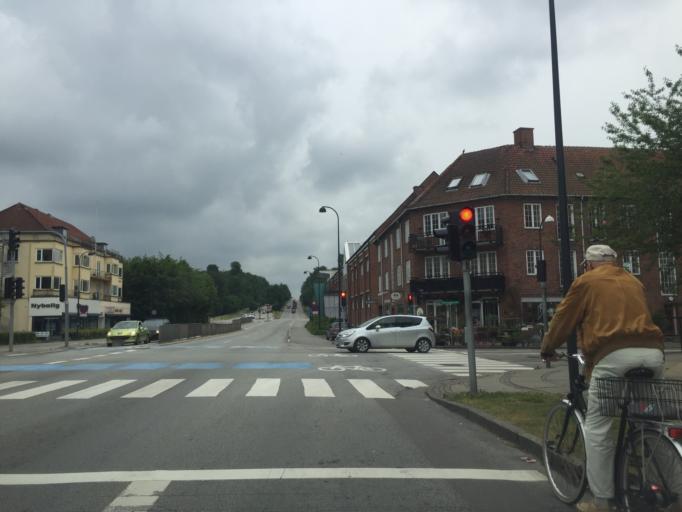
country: DK
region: Capital Region
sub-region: Rudersdal Kommune
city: Holte
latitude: 55.8126
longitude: 12.4715
